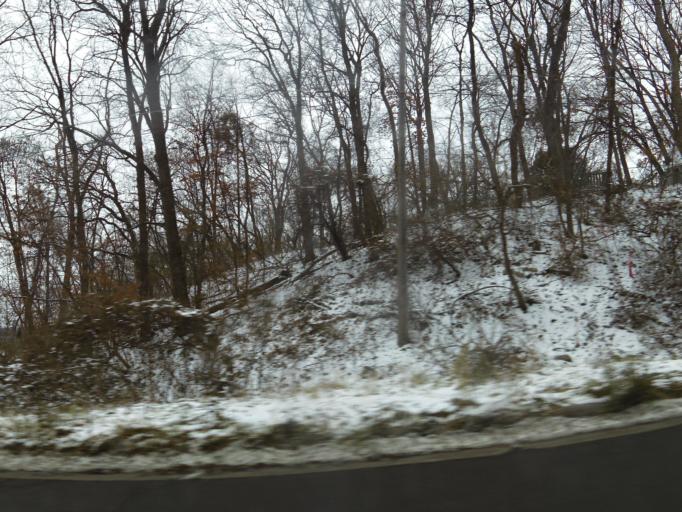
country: US
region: Minnesota
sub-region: Dakota County
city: Mendota Heights
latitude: 44.9058
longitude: -93.1653
